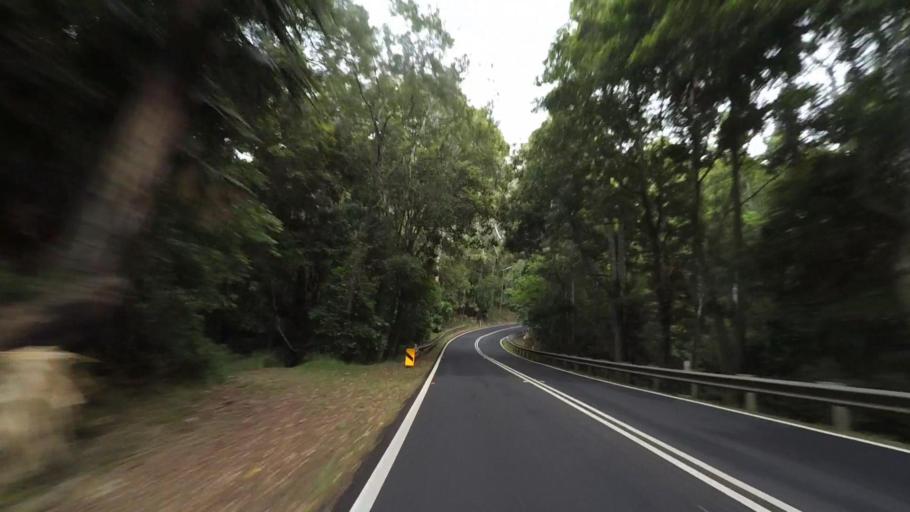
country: AU
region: New South Wales
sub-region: Wollongong
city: Helensburgh
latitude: -34.1567
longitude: 151.0217
